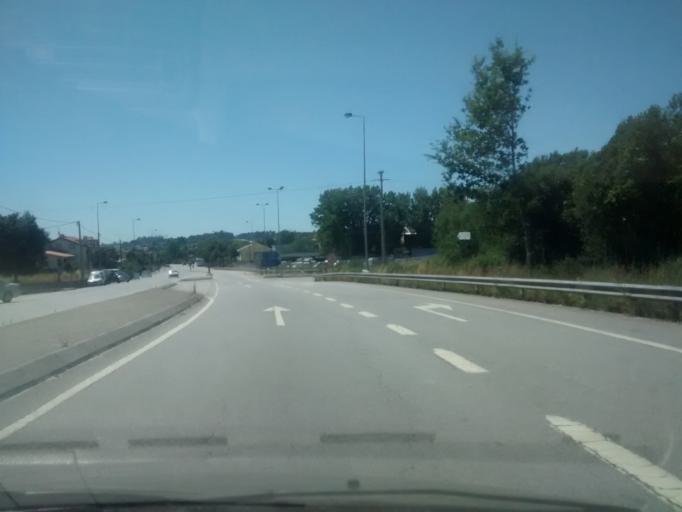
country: PT
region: Braga
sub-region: Braga
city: Oliveira
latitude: 41.5338
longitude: -8.4979
